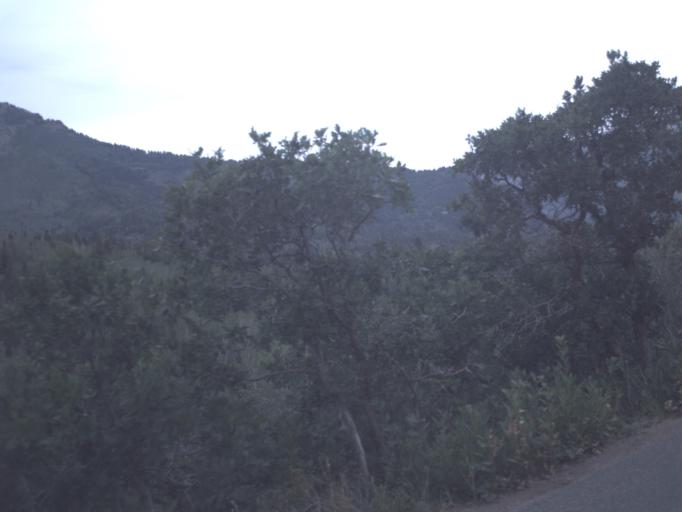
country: US
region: Utah
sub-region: Utah County
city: Lindon
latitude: 40.4377
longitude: -111.6190
